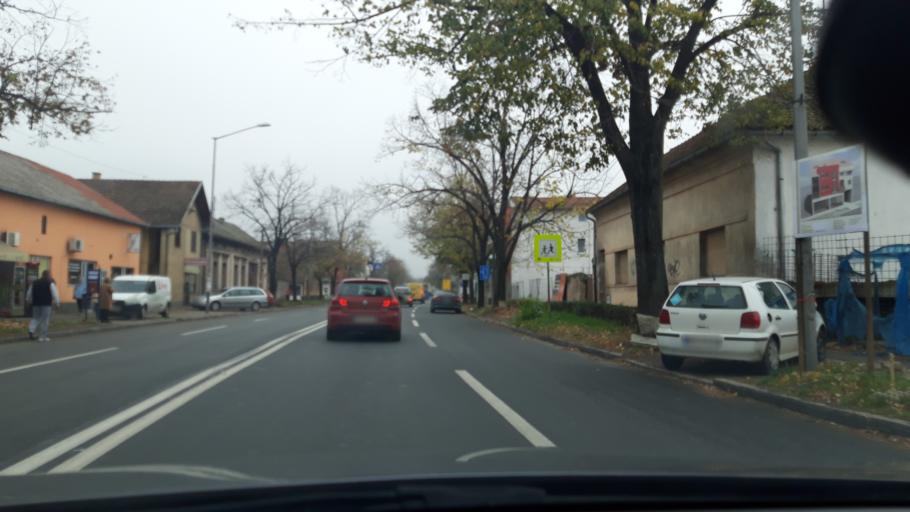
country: RS
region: Autonomna Pokrajina Vojvodina
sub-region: Juznobacki Okrug
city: Petrovaradin
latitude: 45.2466
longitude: 19.8795
